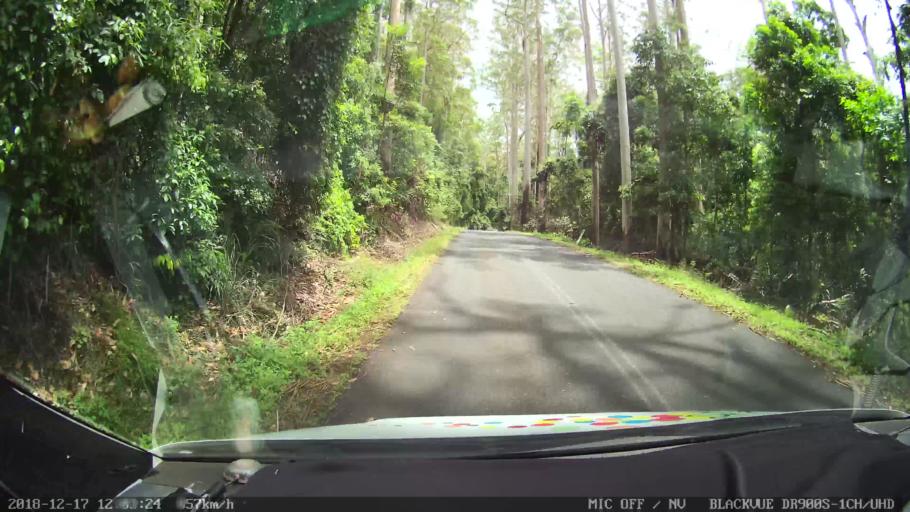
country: AU
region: New South Wales
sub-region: Kyogle
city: Kyogle
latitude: -28.5085
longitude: 152.5682
